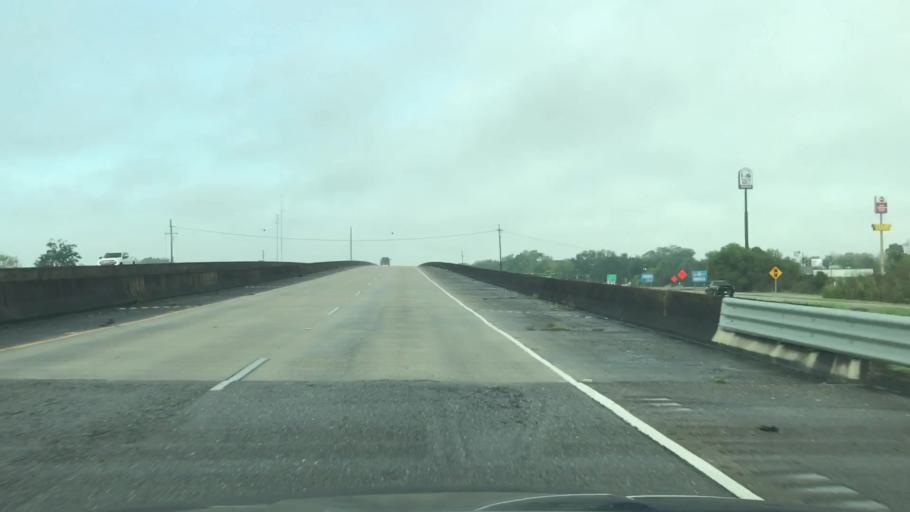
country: US
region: Louisiana
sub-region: Terrebonne Parish
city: Gray
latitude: 29.6801
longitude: -90.7800
